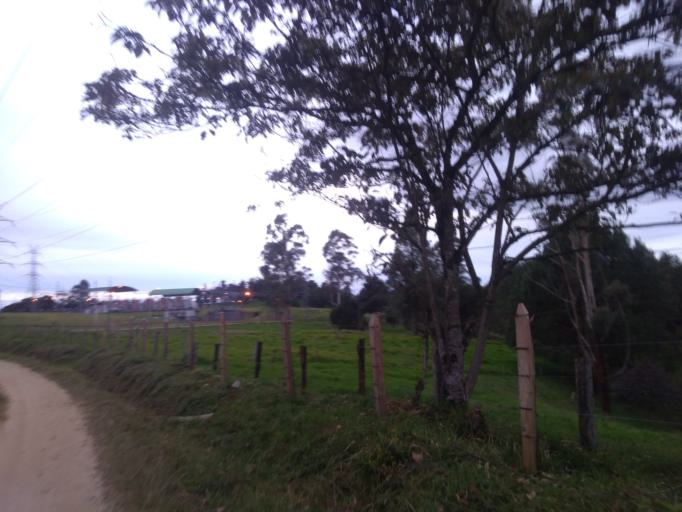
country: CO
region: Antioquia
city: Bello
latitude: 6.3549
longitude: -75.6077
